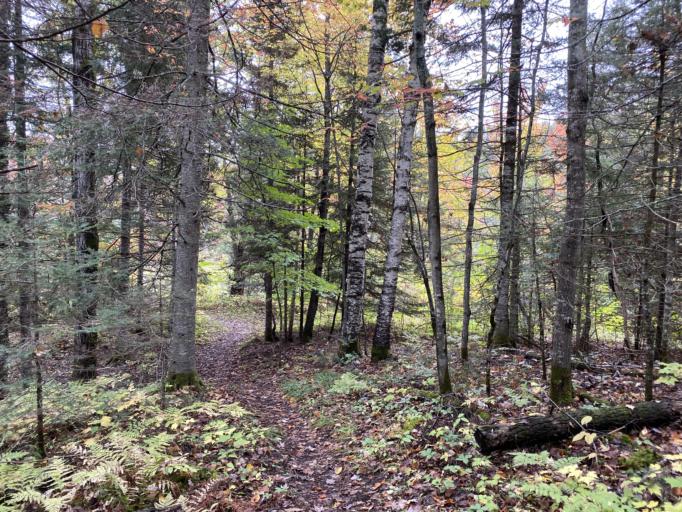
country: US
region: Michigan
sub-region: Marquette County
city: West Ishpeming
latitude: 46.5367
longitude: -88.0006
